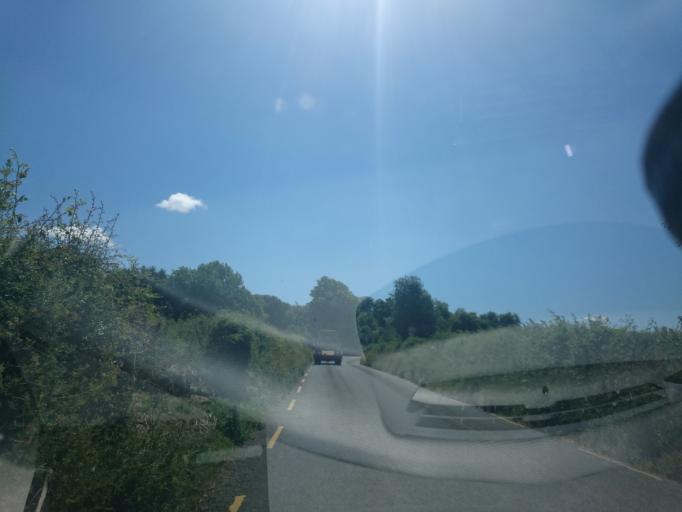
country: IE
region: Leinster
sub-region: Kilkenny
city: Graiguenamanagh
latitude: 52.6064
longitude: -6.9919
